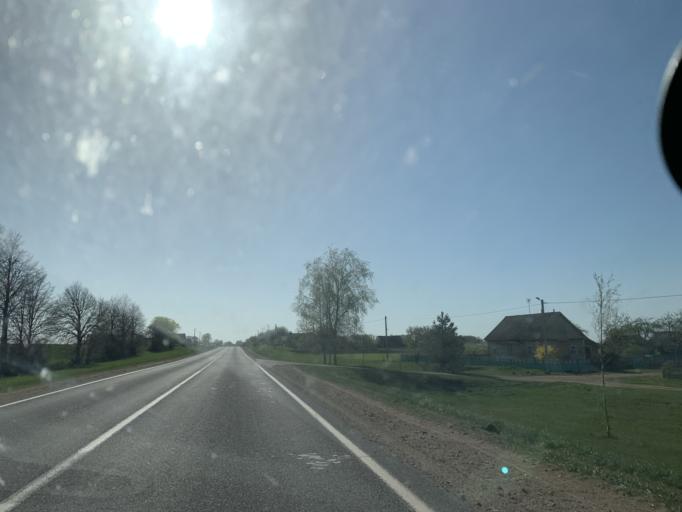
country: BY
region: Minsk
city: Nyasvizh
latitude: 53.2394
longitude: 26.8441
